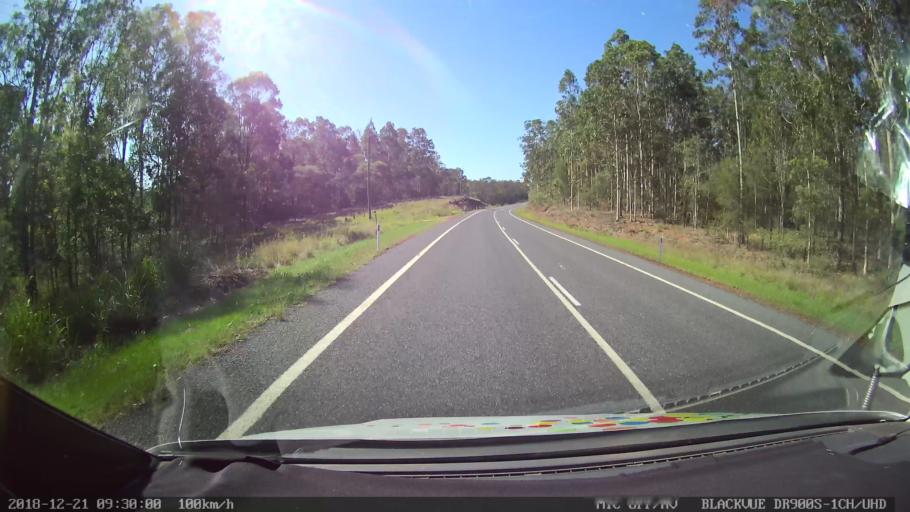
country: AU
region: New South Wales
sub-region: Clarence Valley
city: Maclean
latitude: -29.4401
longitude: 152.9913
